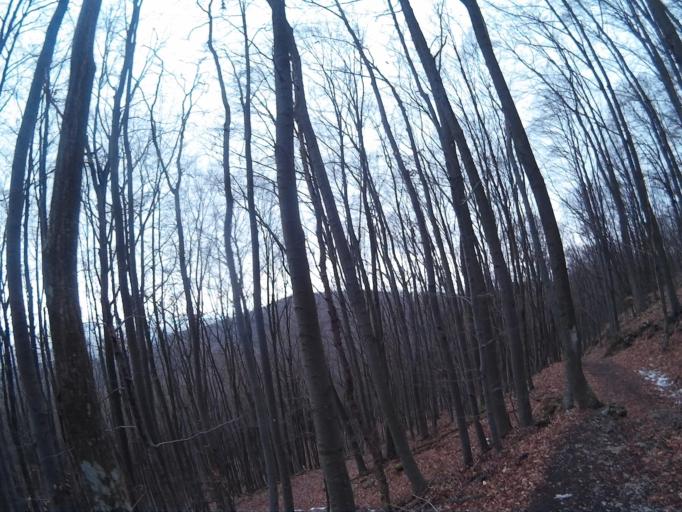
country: HU
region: Heves
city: Belapatfalva
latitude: 48.0566
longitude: 20.4035
